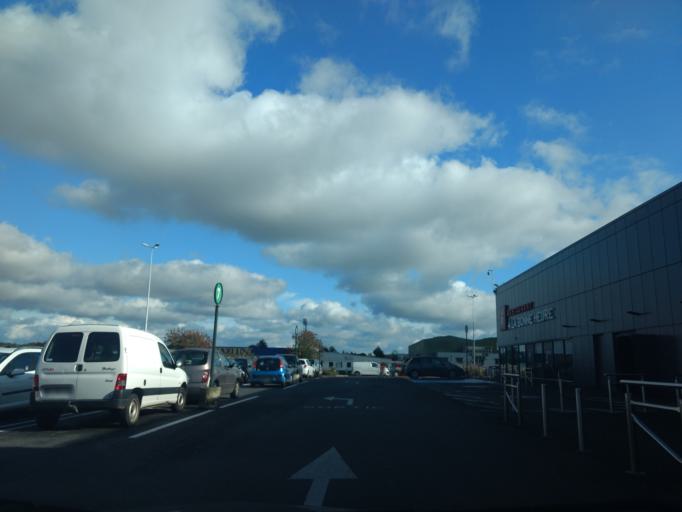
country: FR
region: Poitou-Charentes
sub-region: Departement de la Vienne
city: Chasseneuil-du-Poitou
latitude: 46.6662
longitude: 0.3703
